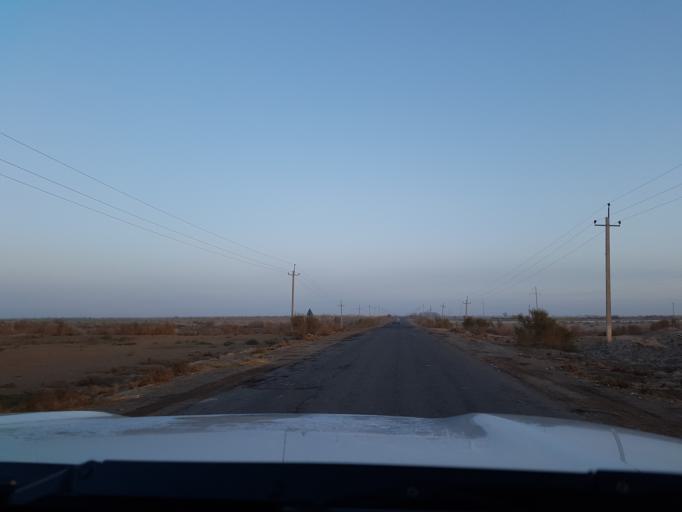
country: TM
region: Dasoguz
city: Koeneuergench
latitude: 41.8211
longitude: 58.7035
